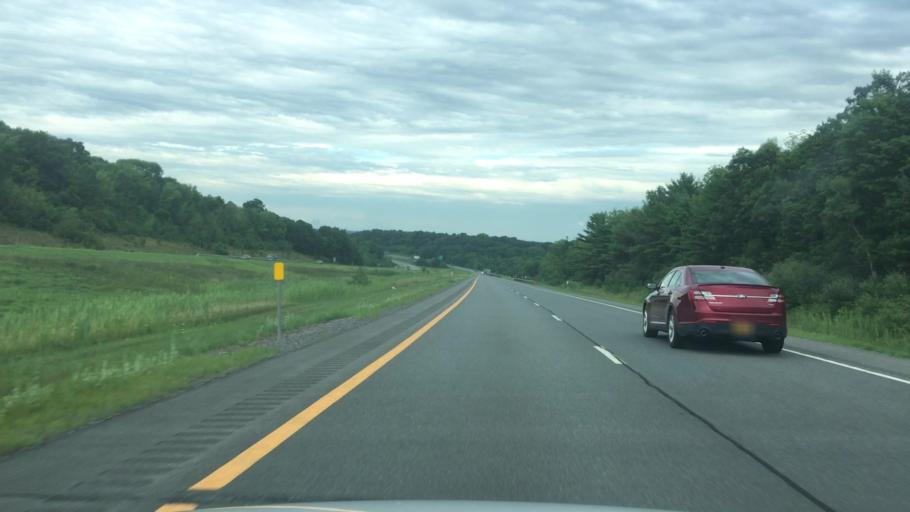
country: US
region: New York
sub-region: Albany County
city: Altamont
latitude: 42.7719
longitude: -74.0638
